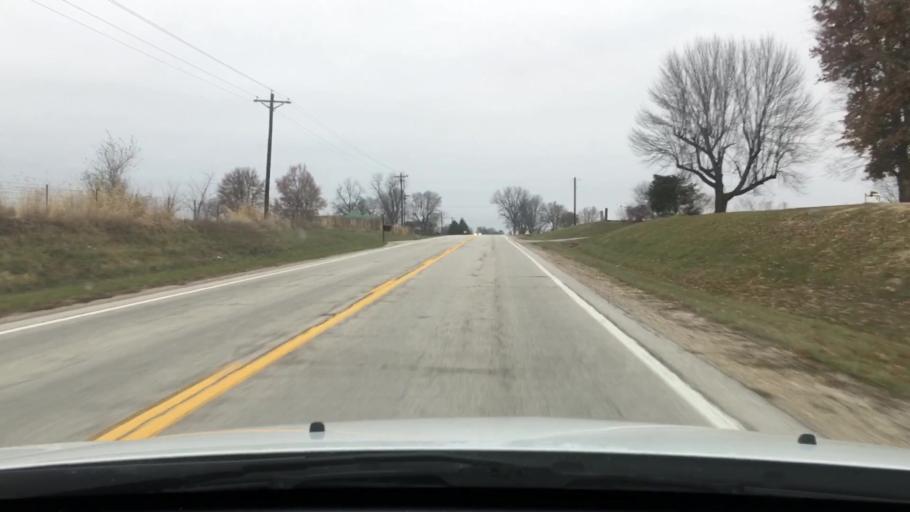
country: US
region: Illinois
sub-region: Pike County
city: Pittsfield
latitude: 39.5532
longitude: -90.9165
